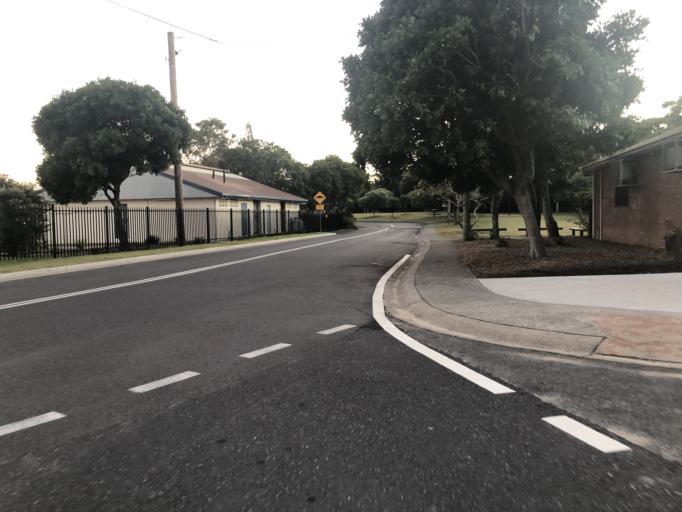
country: AU
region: New South Wales
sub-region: Coffs Harbour
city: Coffs Harbour
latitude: -30.2945
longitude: 153.1380
